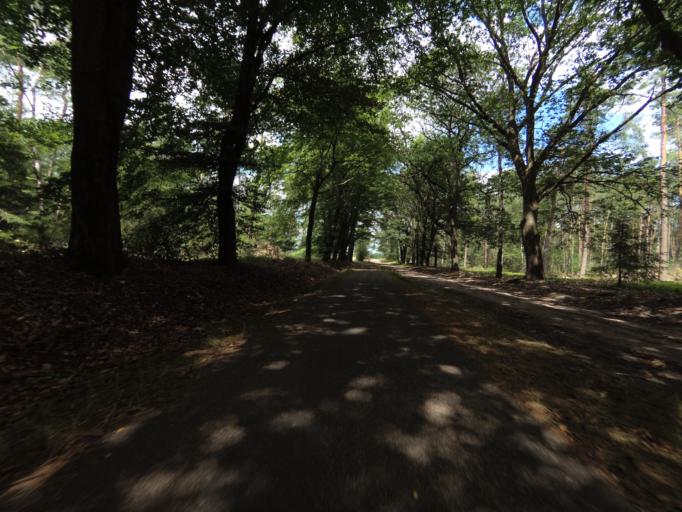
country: NL
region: Overijssel
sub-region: Gemeente Hof van Twente
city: Markelo
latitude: 52.3341
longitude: 6.4504
